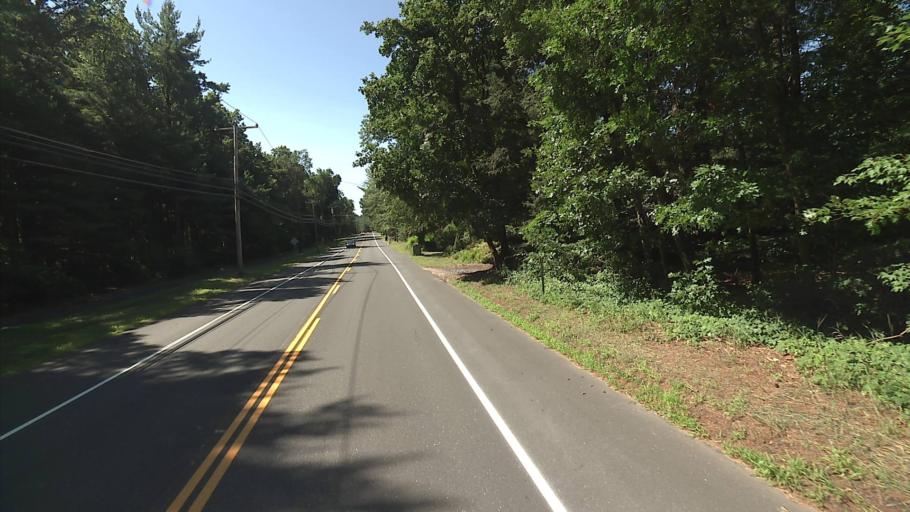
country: US
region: Connecticut
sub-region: Hartford County
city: Salmon Brook
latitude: 41.9261
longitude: -72.7908
